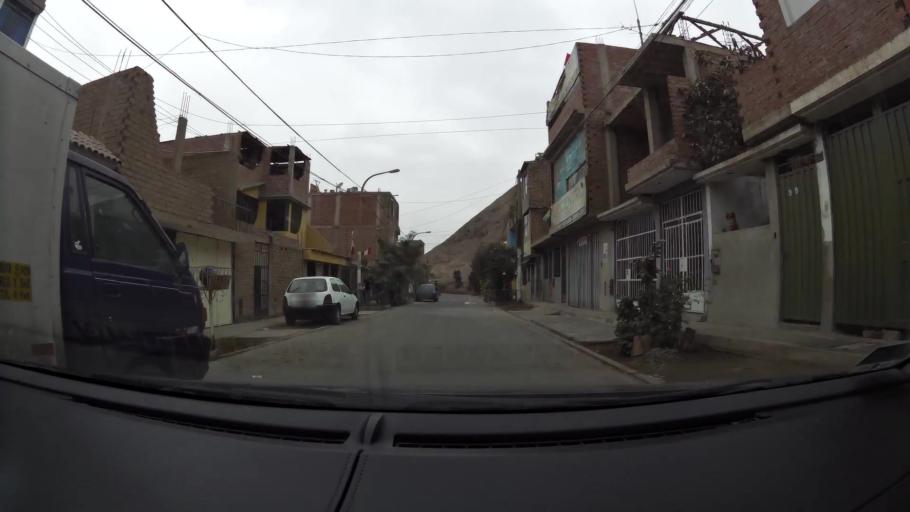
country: PE
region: Lima
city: Ventanilla
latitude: -11.9320
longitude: -77.0858
